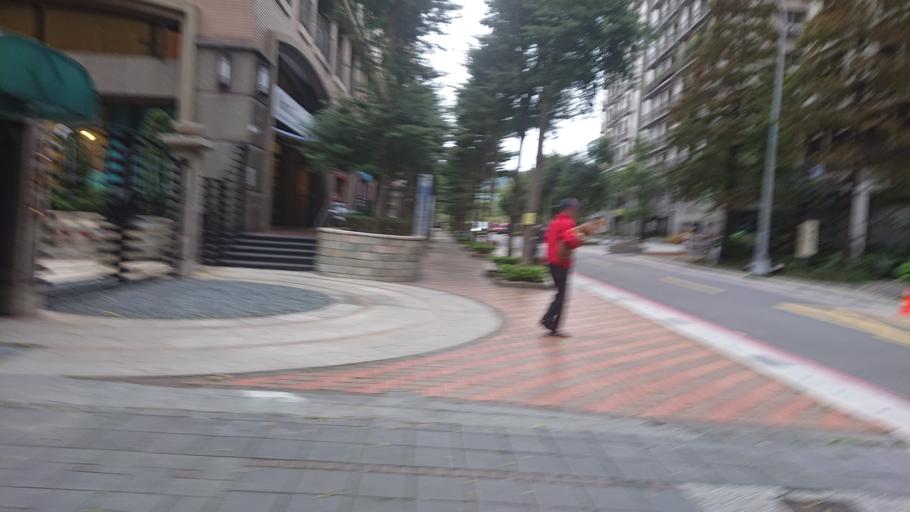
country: TW
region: Taiwan
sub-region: Taoyuan
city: Taoyuan
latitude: 24.9477
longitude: 121.3744
